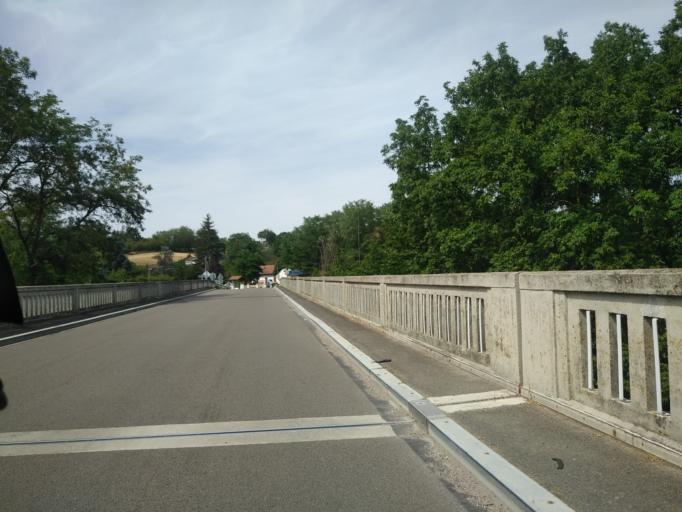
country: FR
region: Auvergne
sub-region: Departement de l'Allier
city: Diou
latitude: 46.5383
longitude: 3.7605
